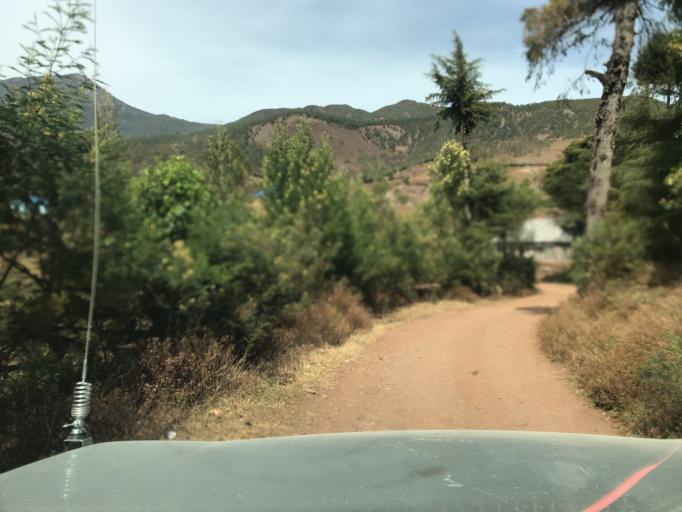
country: TL
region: Ainaro
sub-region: Ainaro
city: Ainaro
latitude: -8.8873
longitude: 125.5200
